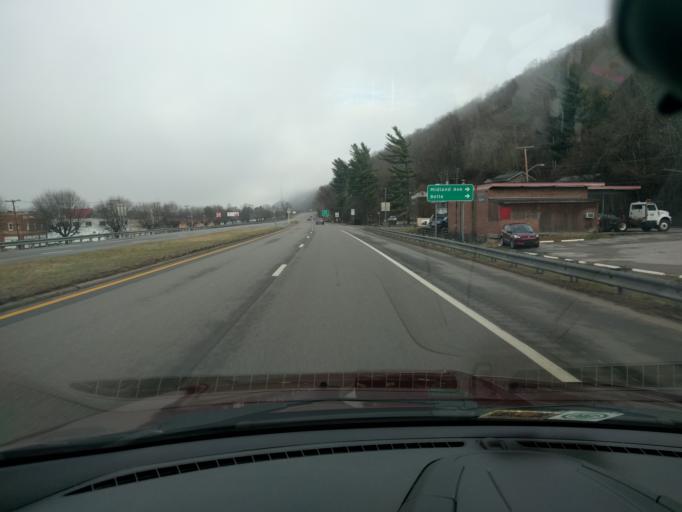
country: US
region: West Virginia
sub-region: Kanawha County
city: Belle
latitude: 38.2310
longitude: -81.5356
